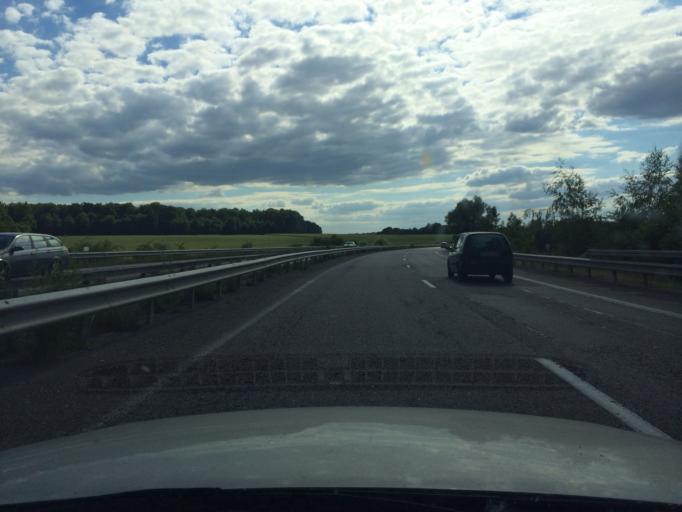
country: FR
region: Lorraine
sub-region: Departement de la Moselle
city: Reding
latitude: 48.7390
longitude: 7.1165
